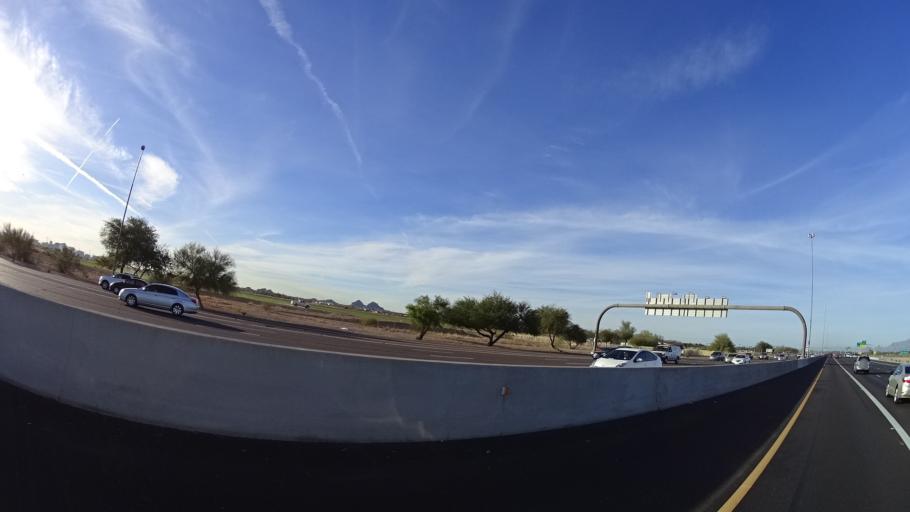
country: US
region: Arizona
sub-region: Maricopa County
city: Tempe
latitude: 33.4423
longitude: -111.8906
